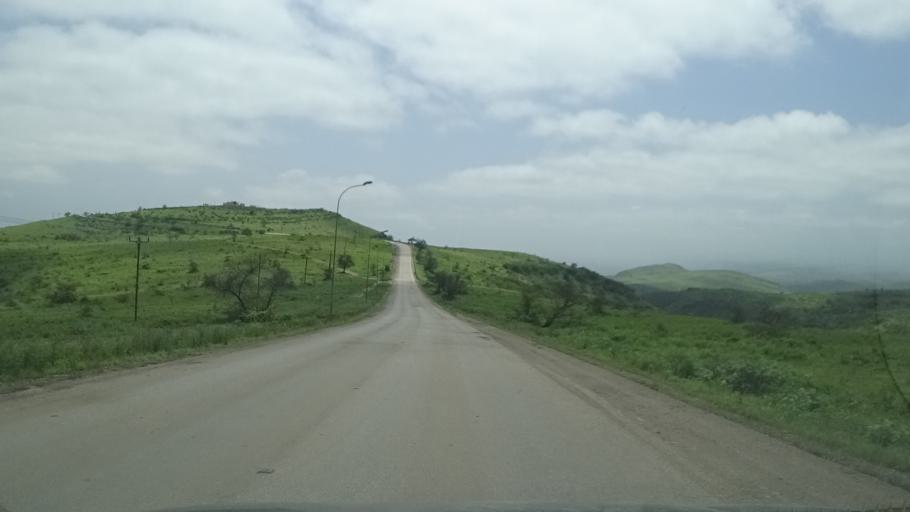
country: OM
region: Zufar
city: Salalah
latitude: 17.1682
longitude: 54.2246
